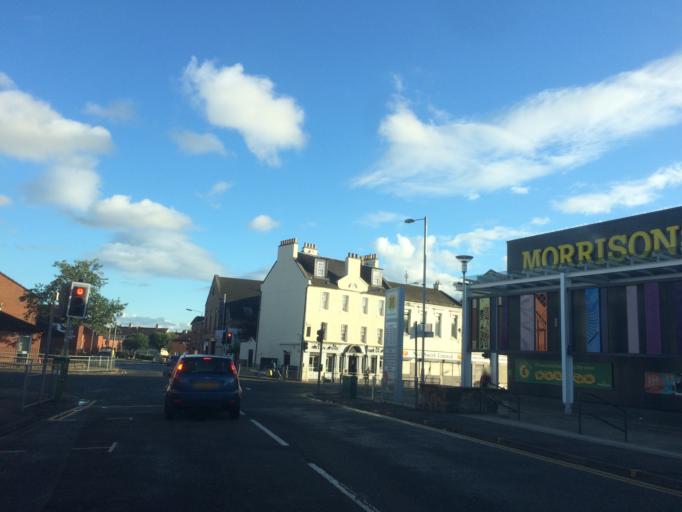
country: GB
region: Scotland
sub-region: Glasgow City
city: Glasgow
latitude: 55.8561
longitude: -4.2328
